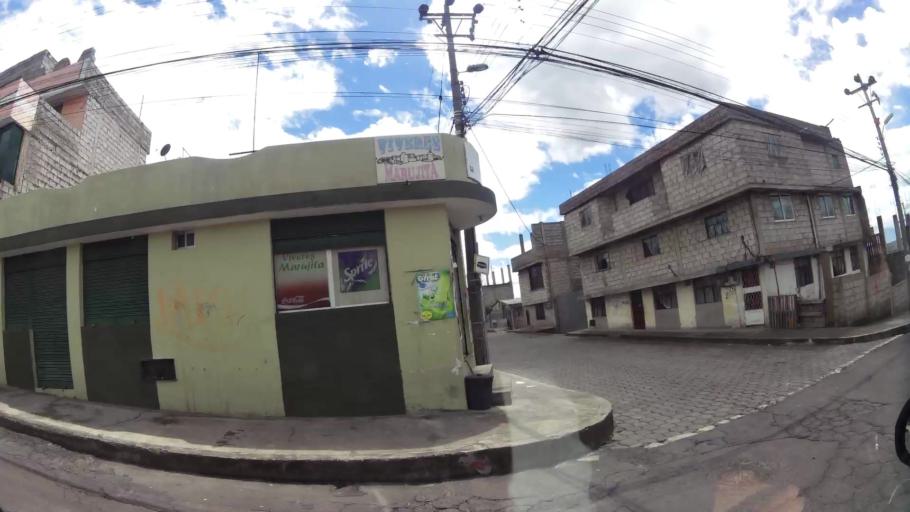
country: EC
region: Pichincha
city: Sangolqui
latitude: -0.3434
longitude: -78.5598
